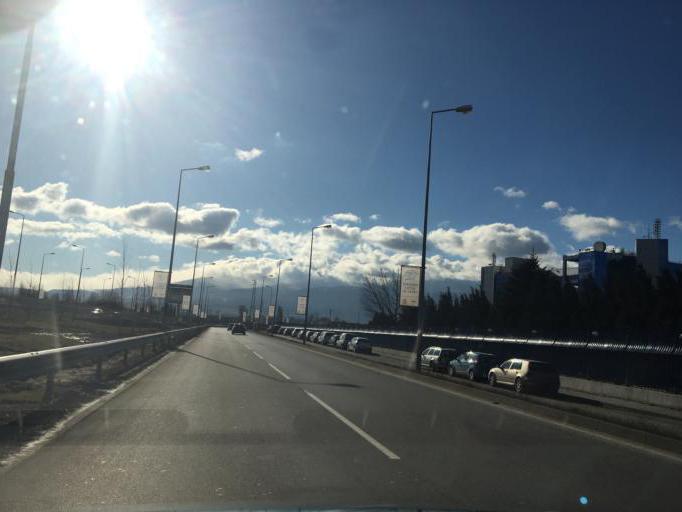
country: BG
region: Sofia-Capital
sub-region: Stolichna Obshtina
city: Sofia
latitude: 42.6856
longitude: 23.4118
